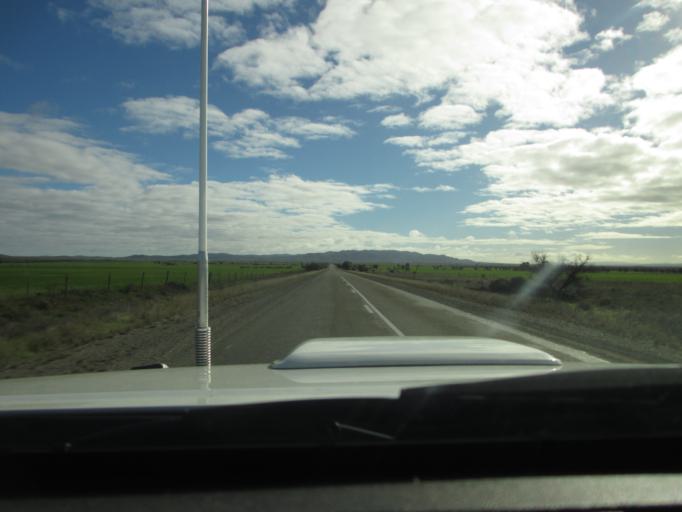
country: AU
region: South Australia
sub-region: Peterborough
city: Peterborough
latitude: -32.6834
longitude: 138.6084
